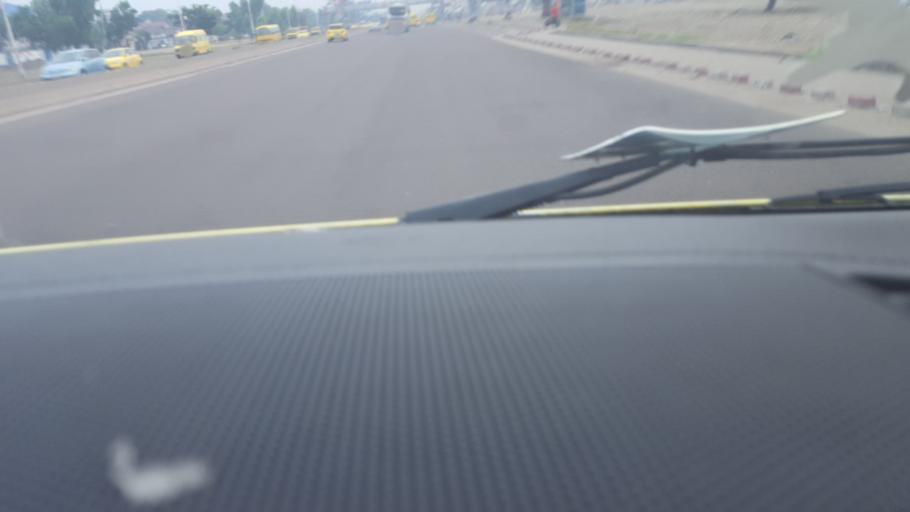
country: CD
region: Kinshasa
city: Kinshasa
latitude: -4.3548
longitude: 15.3370
